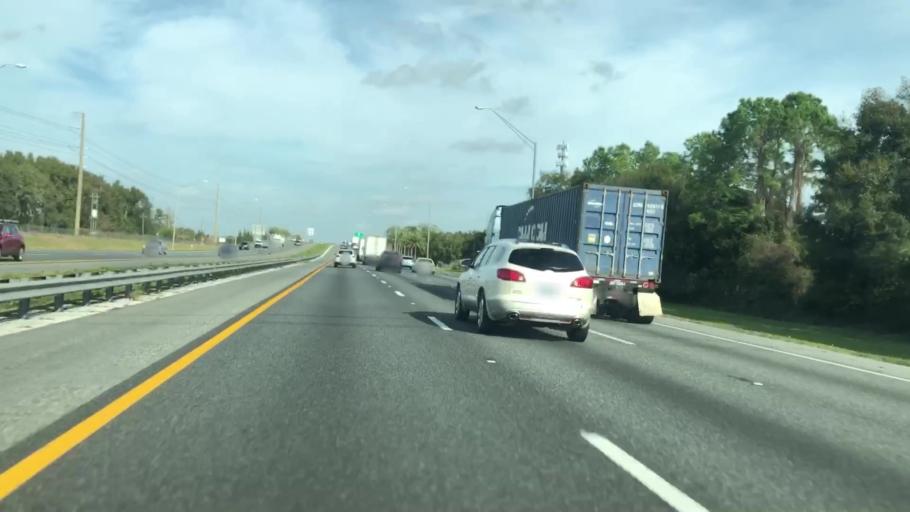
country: US
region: Florida
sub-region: Marion County
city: Ocala
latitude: 29.1637
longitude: -82.1846
